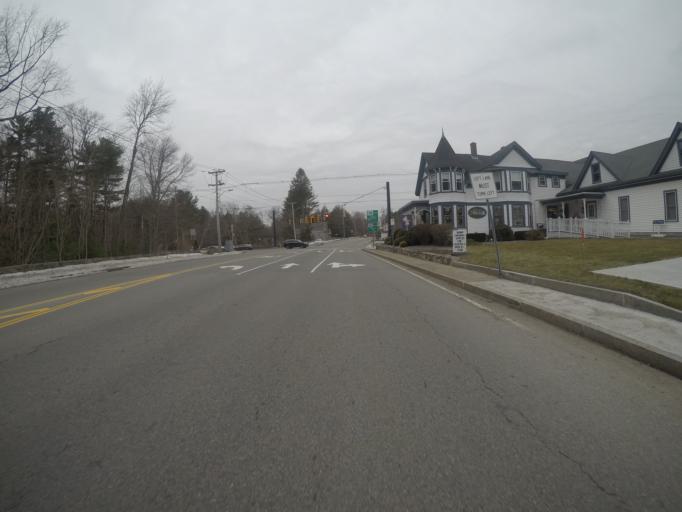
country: US
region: Massachusetts
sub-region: Bristol County
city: Easton
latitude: 42.0669
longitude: -71.0866
